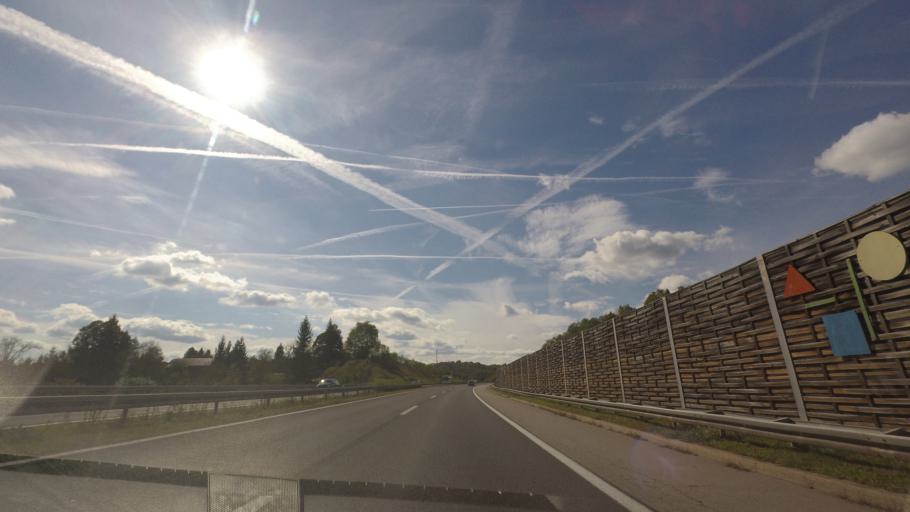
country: HR
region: Karlovacka
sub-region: Grad Karlovac
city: Karlovac
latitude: 45.4662
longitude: 15.4073
